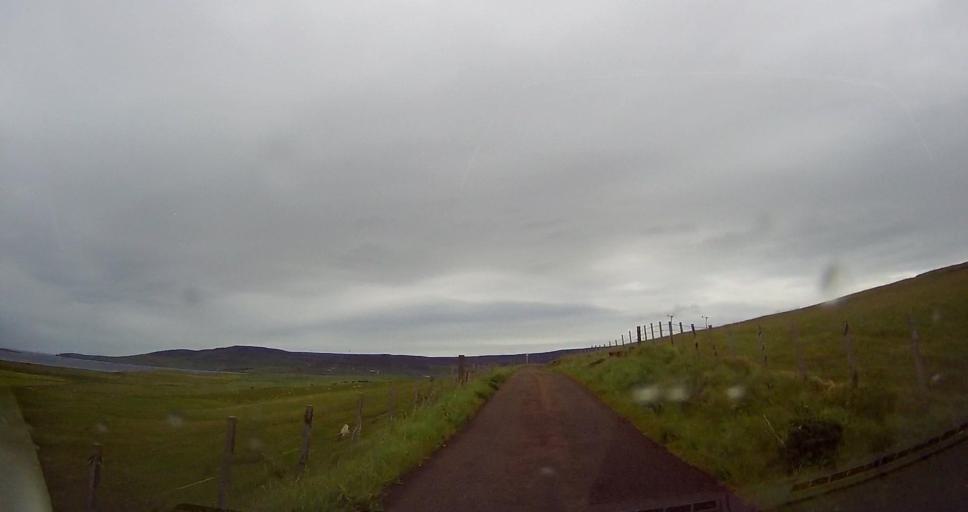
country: GB
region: Scotland
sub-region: Orkney Islands
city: Orkney
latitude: 59.1083
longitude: -3.0819
